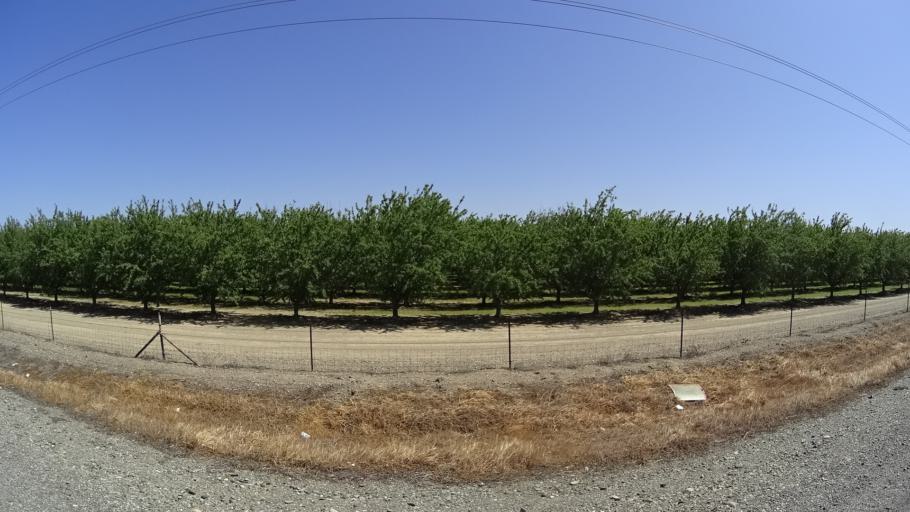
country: US
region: California
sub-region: Glenn County
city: Orland
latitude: 39.6482
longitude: -122.1972
